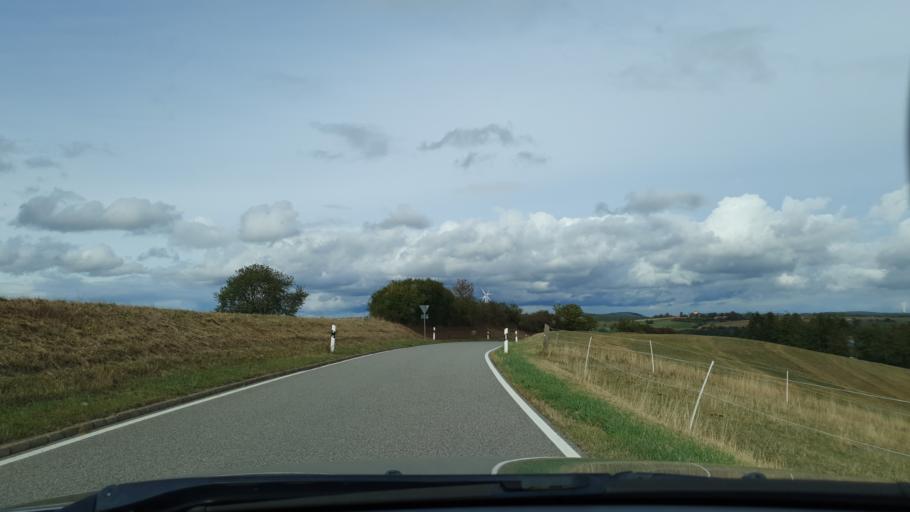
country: DE
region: Rheinland-Pfalz
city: Knopp-Labach
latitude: 49.3392
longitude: 7.4936
